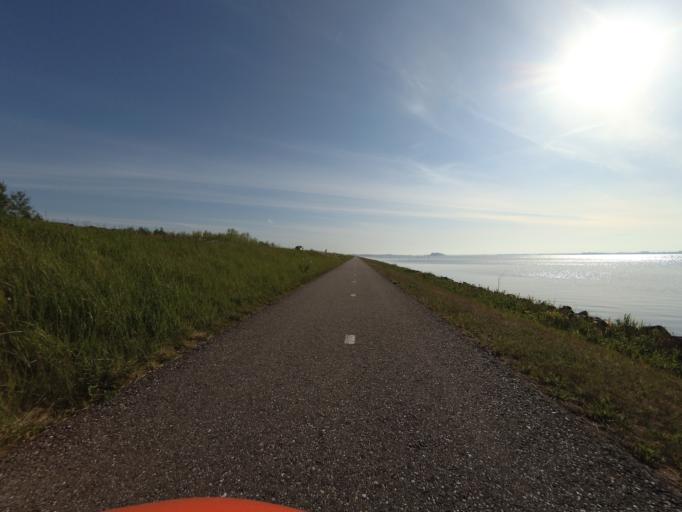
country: NL
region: Flevoland
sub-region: Gemeente Dronten
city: Biddinghuizen
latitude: 52.4012
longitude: 5.6719
